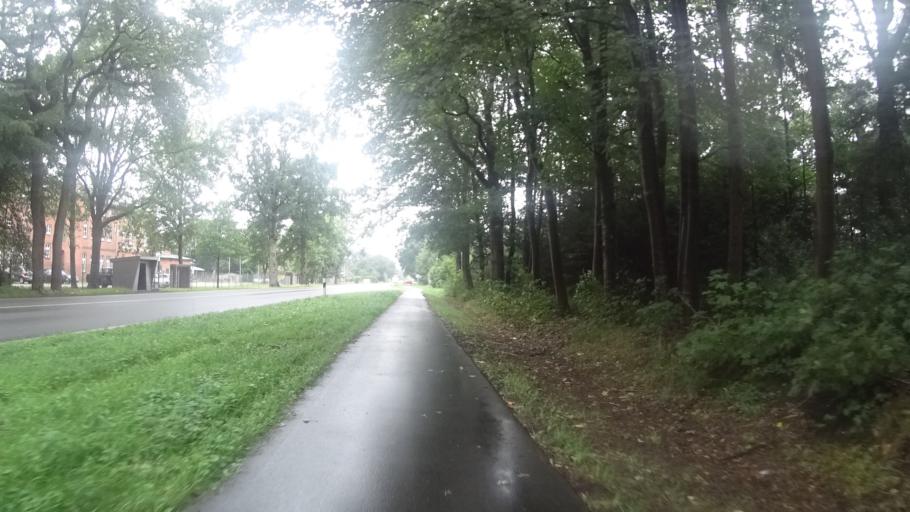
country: DE
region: Lower Saxony
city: Holtland
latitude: 53.2908
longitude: 7.5848
